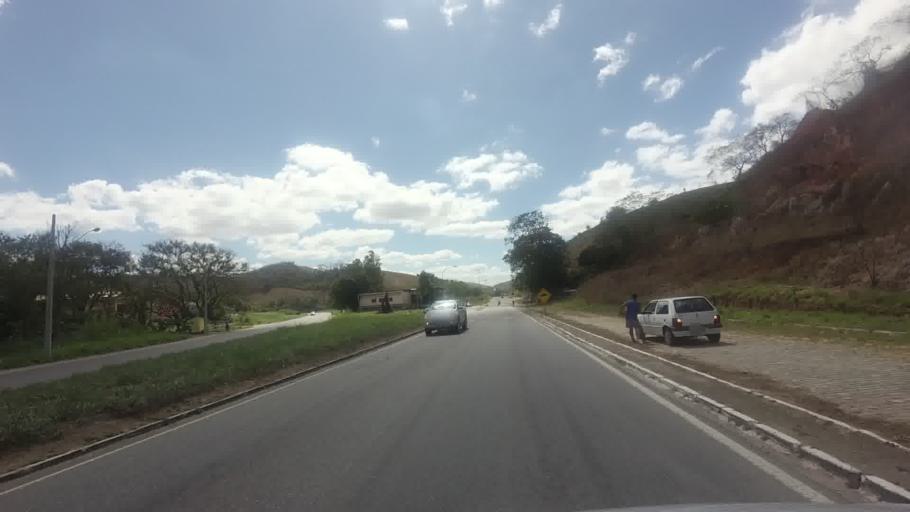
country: BR
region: Minas Gerais
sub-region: Alem Paraiba
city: Alem Paraiba
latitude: -21.8596
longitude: -42.6632
